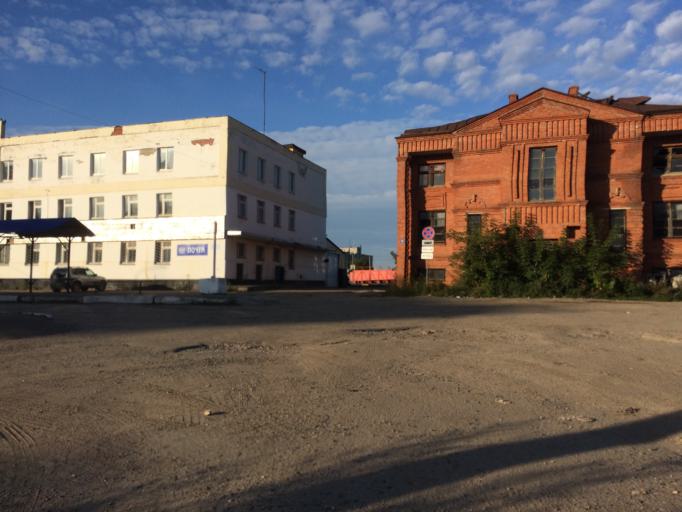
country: RU
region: Mariy-El
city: Yoshkar-Ola
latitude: 56.6232
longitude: 47.8793
